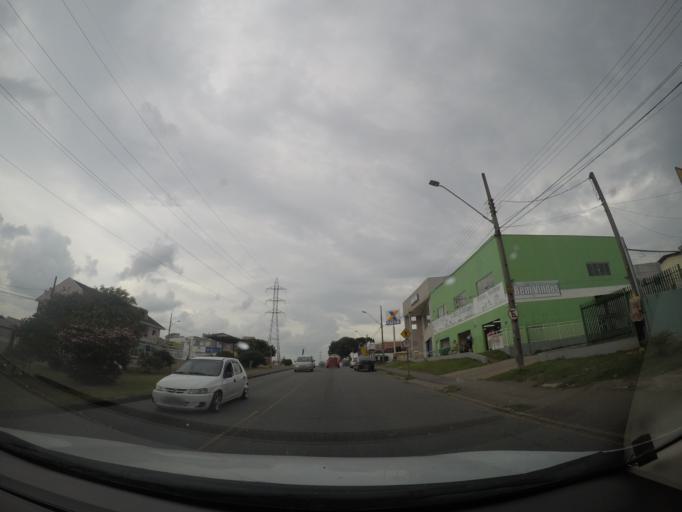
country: BR
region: Parana
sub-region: Sao Jose Dos Pinhais
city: Sao Jose dos Pinhais
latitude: -25.5523
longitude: -49.2522
